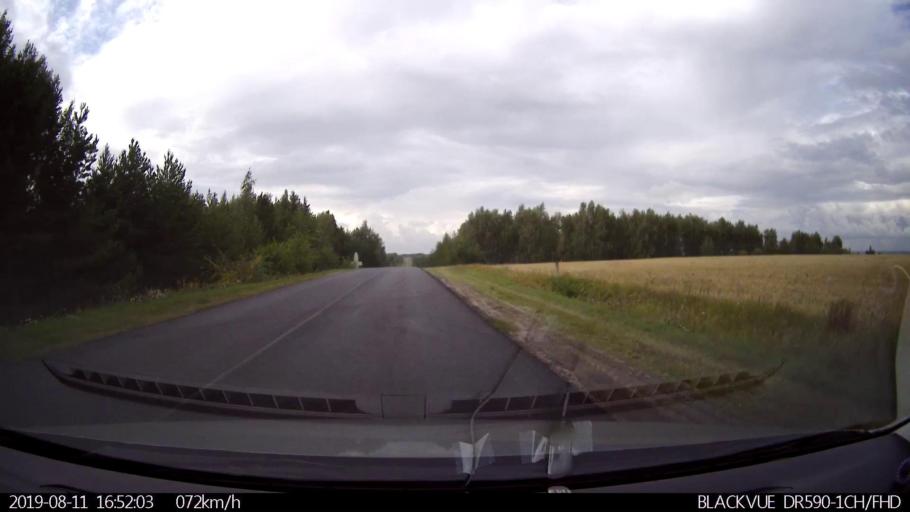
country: RU
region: Ulyanovsk
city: Mayna
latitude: 54.2435
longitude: 47.6753
